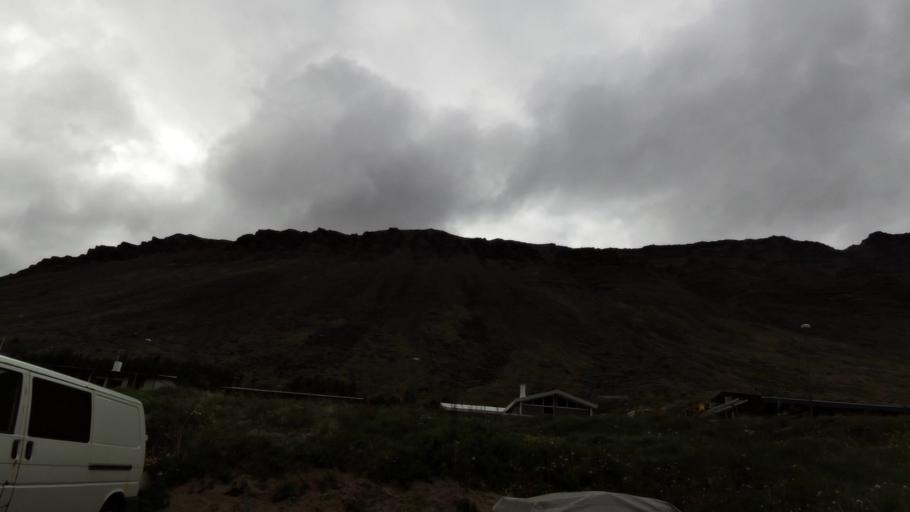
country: IS
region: Westfjords
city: Isafjoerdur
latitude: 66.0800
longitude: -23.1256
